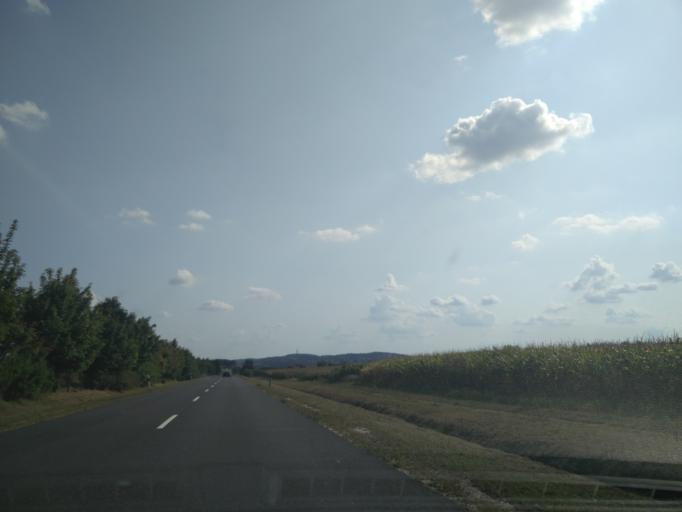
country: HU
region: Zala
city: Zalaegerszeg
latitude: 46.8769
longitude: 16.8305
